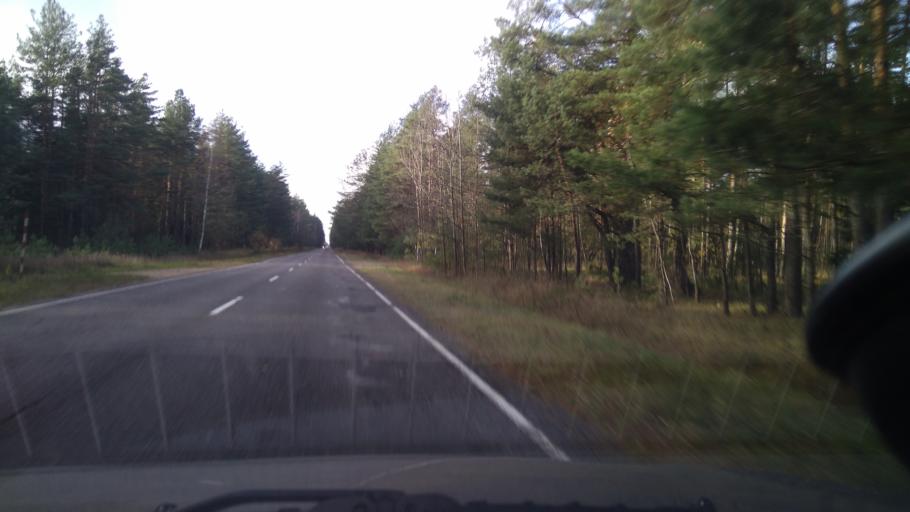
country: BY
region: Minsk
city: Slutsk
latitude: 53.2300
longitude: 27.6935
